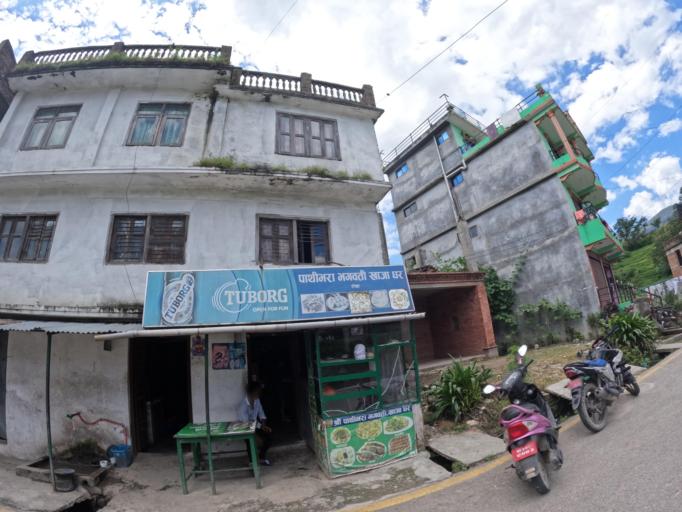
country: NP
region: Central Region
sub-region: Bagmati Zone
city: Kathmandu
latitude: 27.7727
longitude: 85.3303
